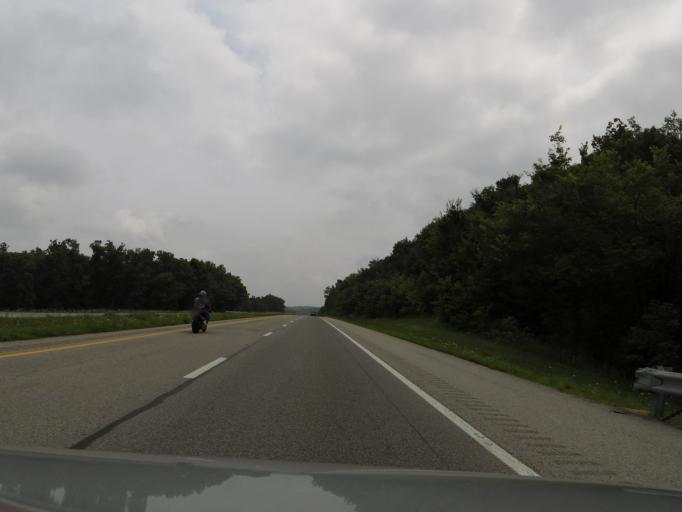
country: US
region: Kentucky
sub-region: Ohio County
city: Beaver Dam
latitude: 37.3323
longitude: -86.9613
